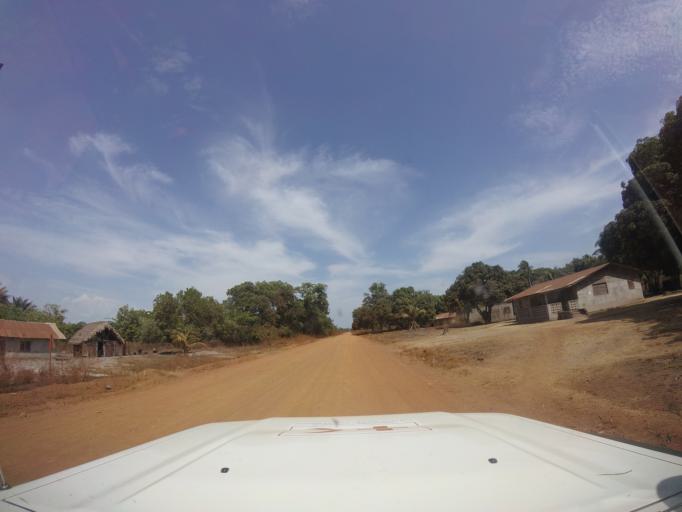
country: LR
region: Grand Cape Mount
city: Robertsport
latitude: 6.7057
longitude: -11.3321
